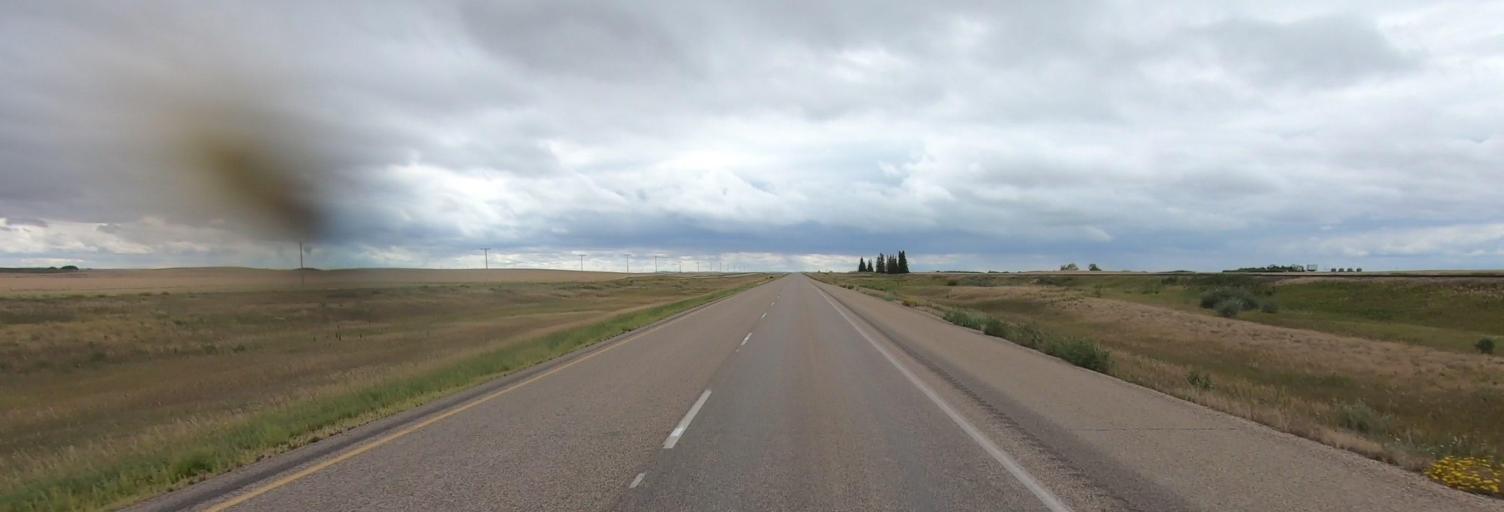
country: CA
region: Saskatchewan
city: Gravelbourg
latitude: 50.4394
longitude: -106.9085
